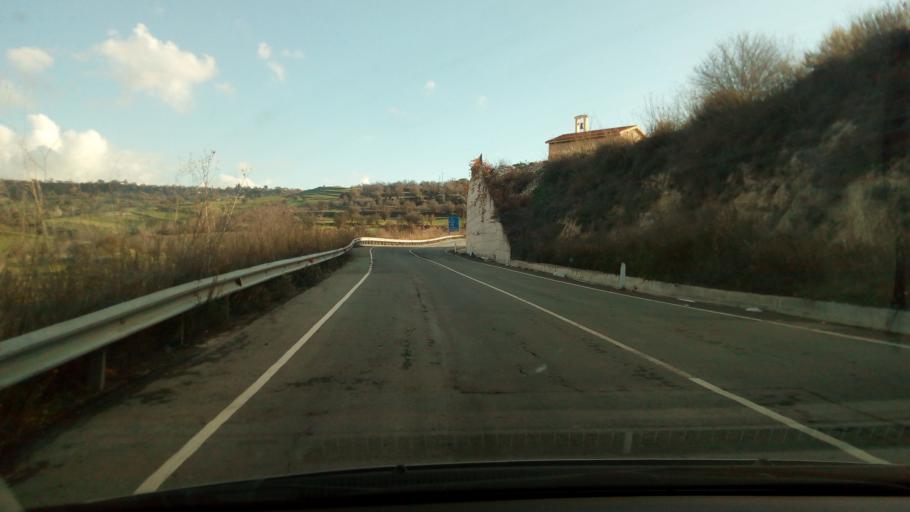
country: CY
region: Pafos
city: Tala
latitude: 34.9371
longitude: 32.5161
